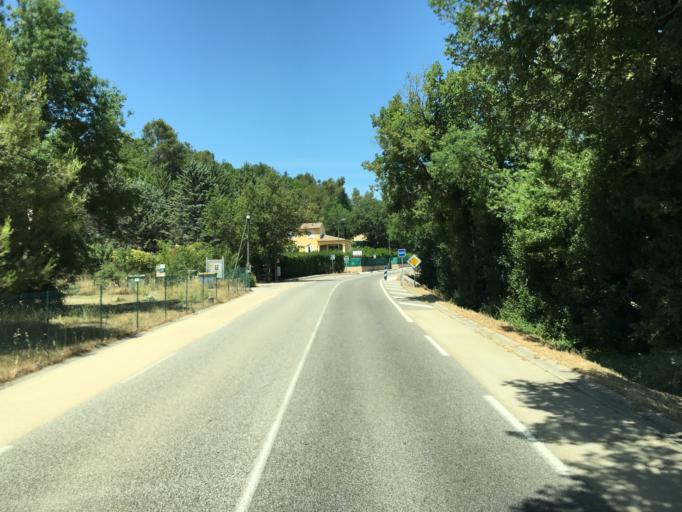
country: FR
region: Provence-Alpes-Cote d'Azur
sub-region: Departement du Var
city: Saint-Maximin-la-Sainte-Baume
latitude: 43.4737
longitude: 5.8342
